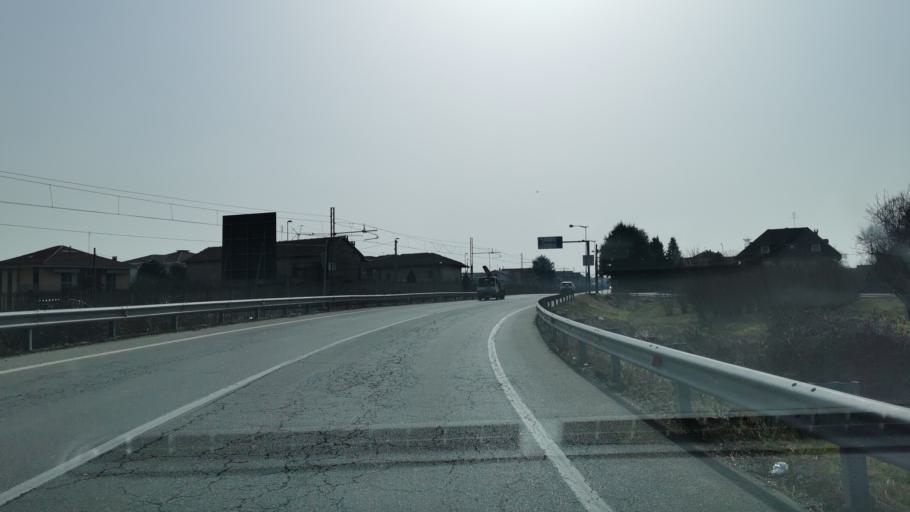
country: IT
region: Piedmont
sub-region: Provincia di Torino
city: Volpiano
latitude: 45.2097
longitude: 7.7804
